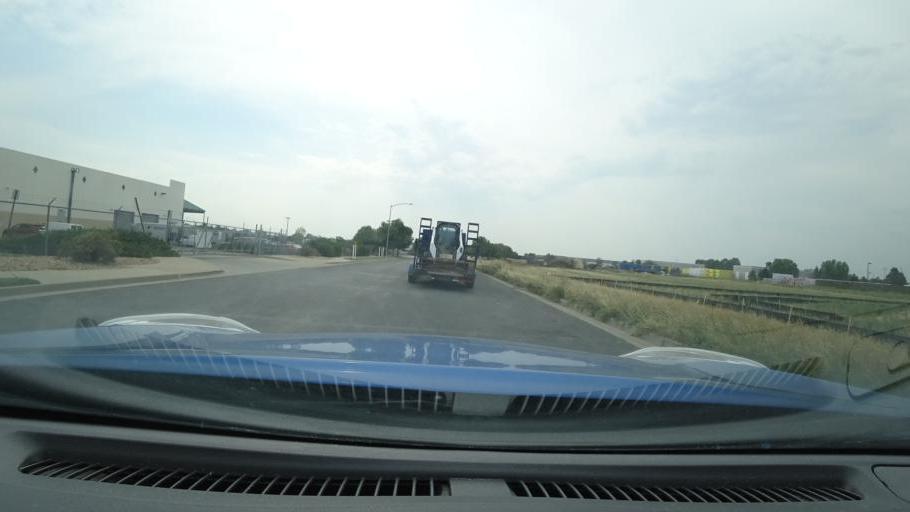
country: US
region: Colorado
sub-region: Adams County
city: Aurora
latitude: 39.7501
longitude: -104.7806
